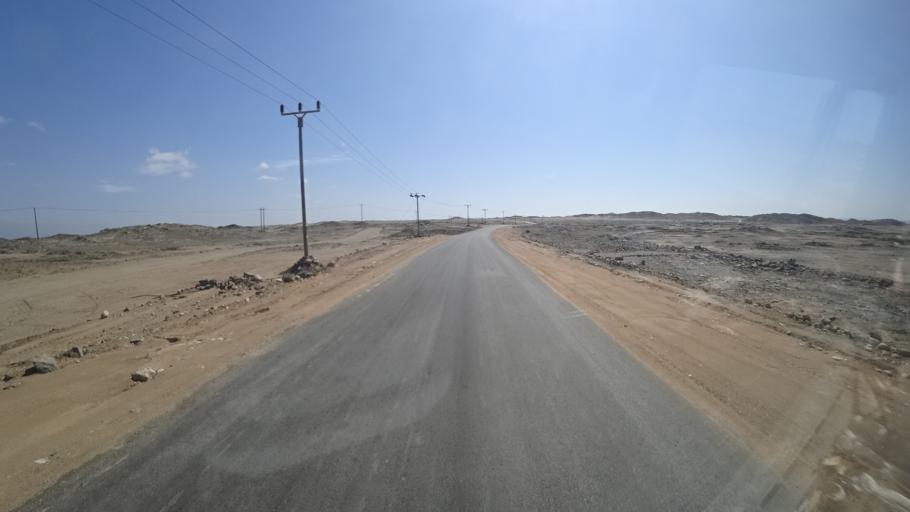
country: OM
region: Zufar
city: Salalah
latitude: 16.9663
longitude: 54.7530
